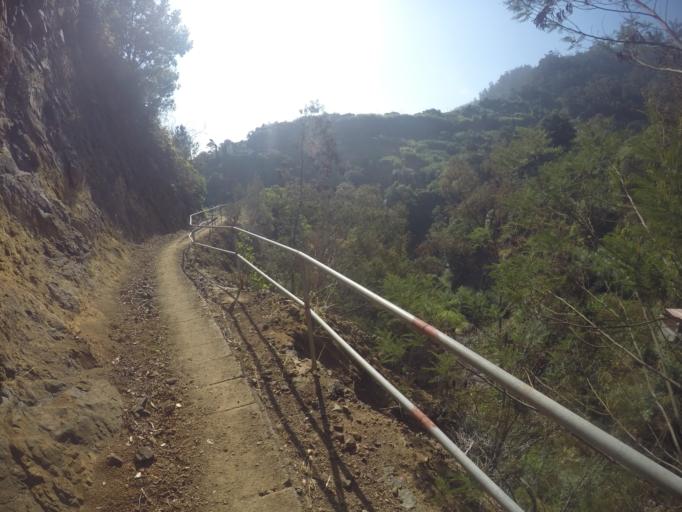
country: PT
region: Madeira
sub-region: Santana
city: Santana
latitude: 32.7665
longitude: -16.8194
